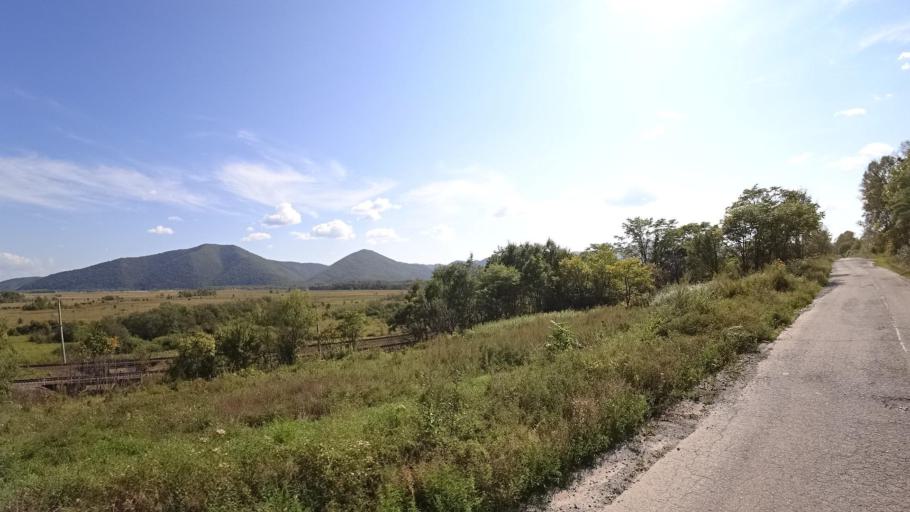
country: RU
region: Jewish Autonomous Oblast
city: Birakan
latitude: 48.9986
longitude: 131.8520
